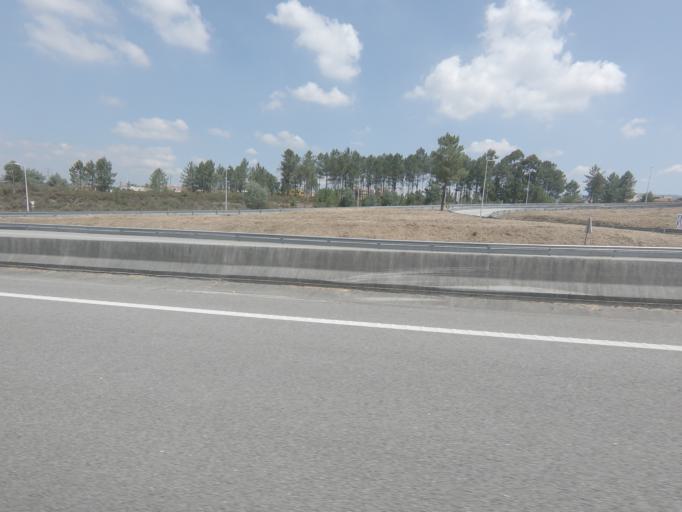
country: PT
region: Porto
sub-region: Valongo
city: Campo
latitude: 41.1840
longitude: -8.4523
